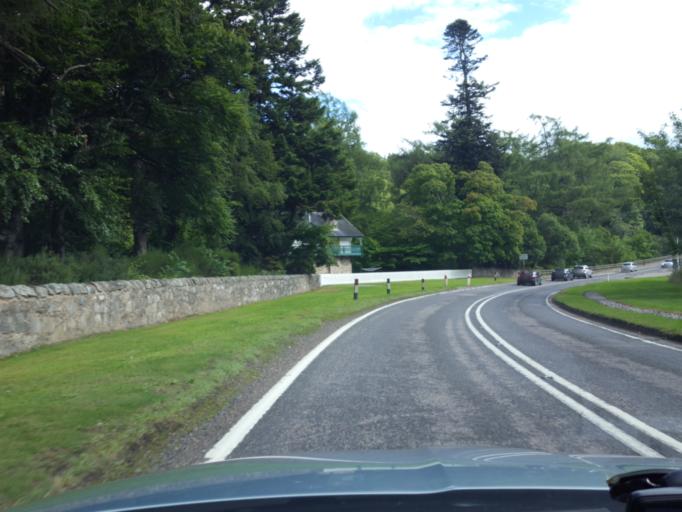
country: GB
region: Scotland
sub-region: Moray
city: Rothes
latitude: 57.4069
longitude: -3.3636
